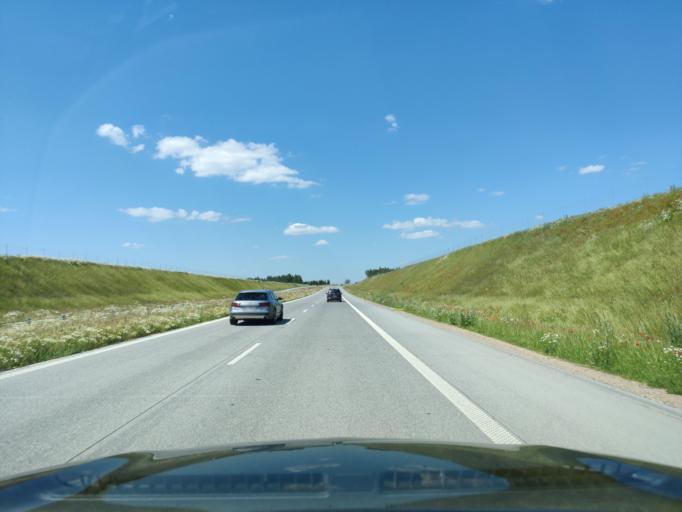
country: PL
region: Masovian Voivodeship
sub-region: Powiat mlawski
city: Wisniewo
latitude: 53.0044
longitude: 20.3412
